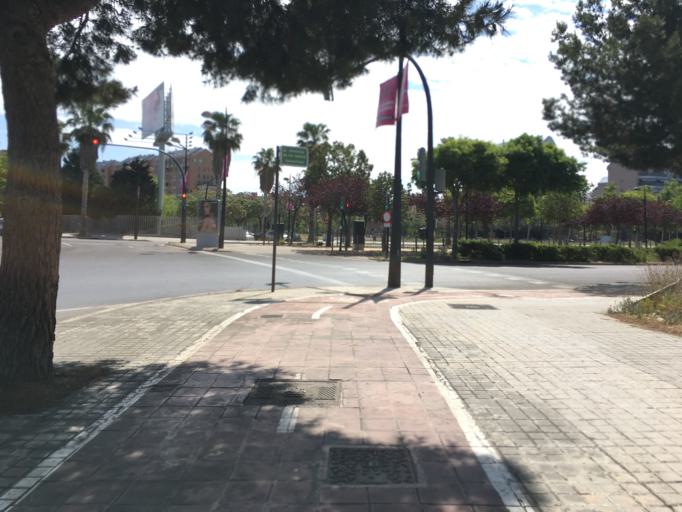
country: ES
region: Valencia
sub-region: Provincia de Valencia
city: Mislata
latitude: 39.4803
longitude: -0.4076
